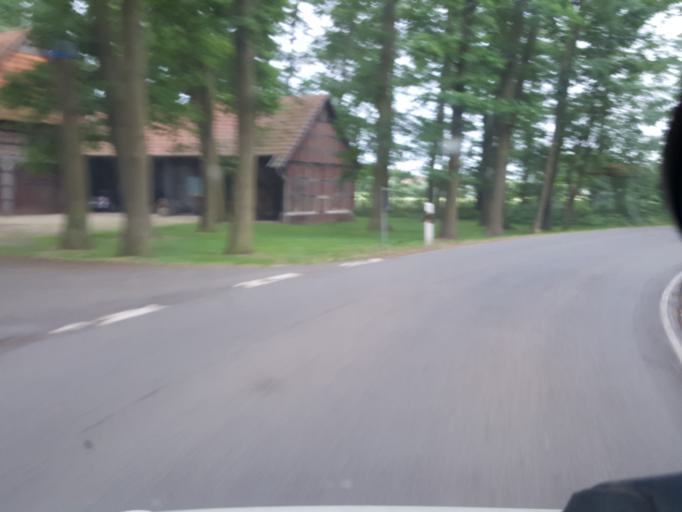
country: DE
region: North Rhine-Westphalia
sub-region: Regierungsbezirk Detmold
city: Minden
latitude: 52.3576
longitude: 8.8564
